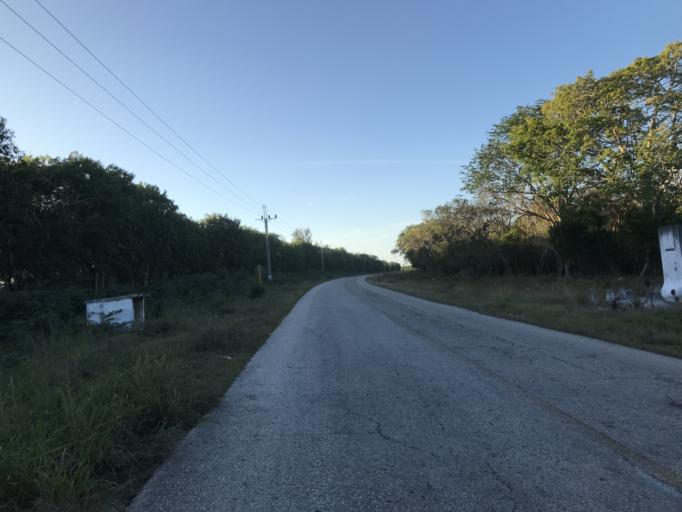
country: CU
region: Cienfuegos
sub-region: Municipio de Aguada de Pasajeros
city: Aguada de Pasajeros
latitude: 22.0695
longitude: -81.0523
